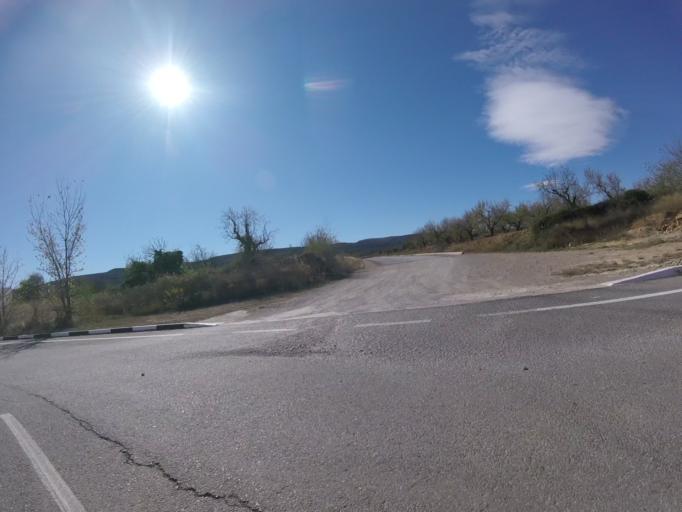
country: ES
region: Valencia
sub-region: Provincia de Castello
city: Albocasser
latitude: 40.3579
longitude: 0.0181
